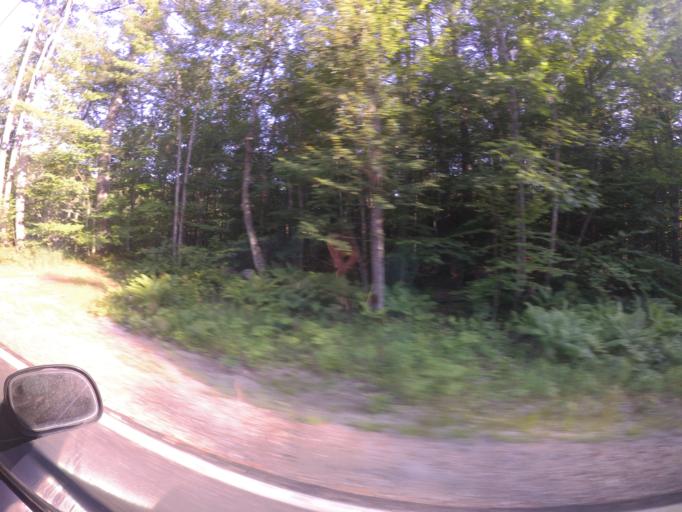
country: US
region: Maine
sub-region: Cumberland County
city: Raymond
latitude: 43.8944
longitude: -70.4448
